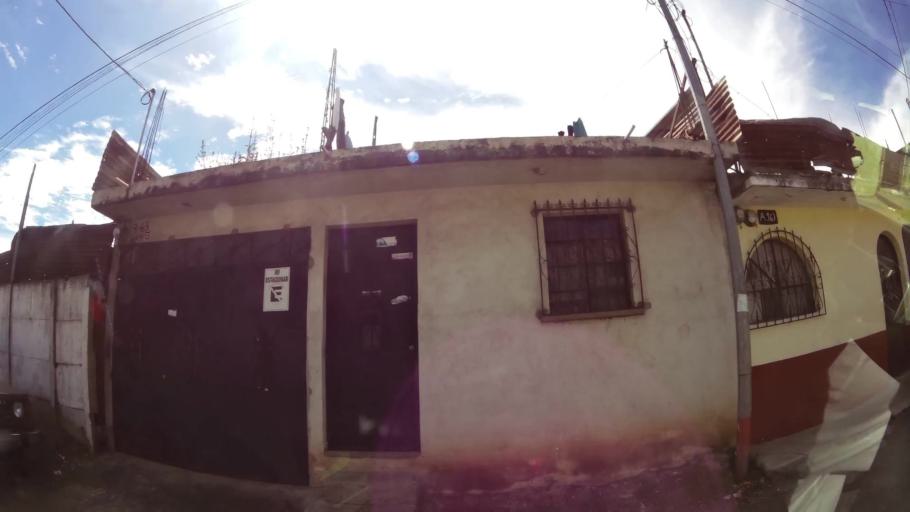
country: GT
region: Guatemala
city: Mixco
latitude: 14.6445
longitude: -90.5952
